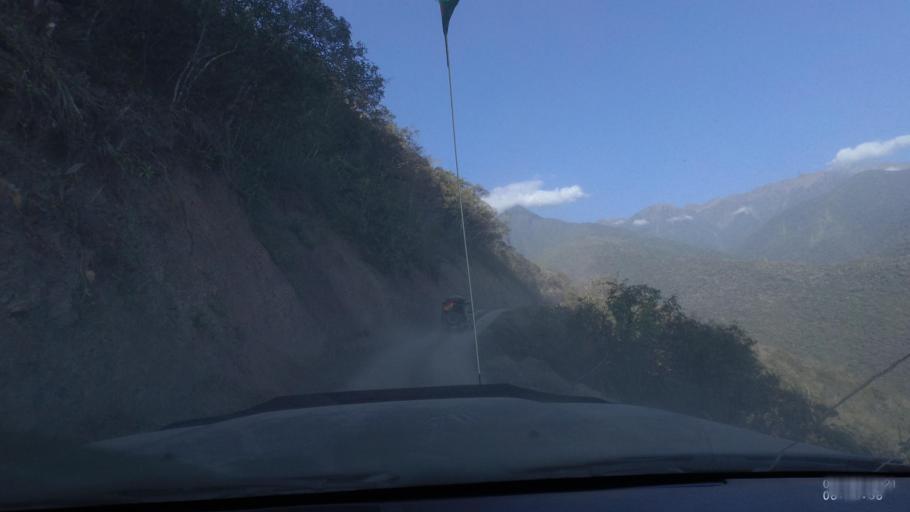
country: BO
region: La Paz
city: Quime
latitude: -16.5174
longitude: -66.7685
